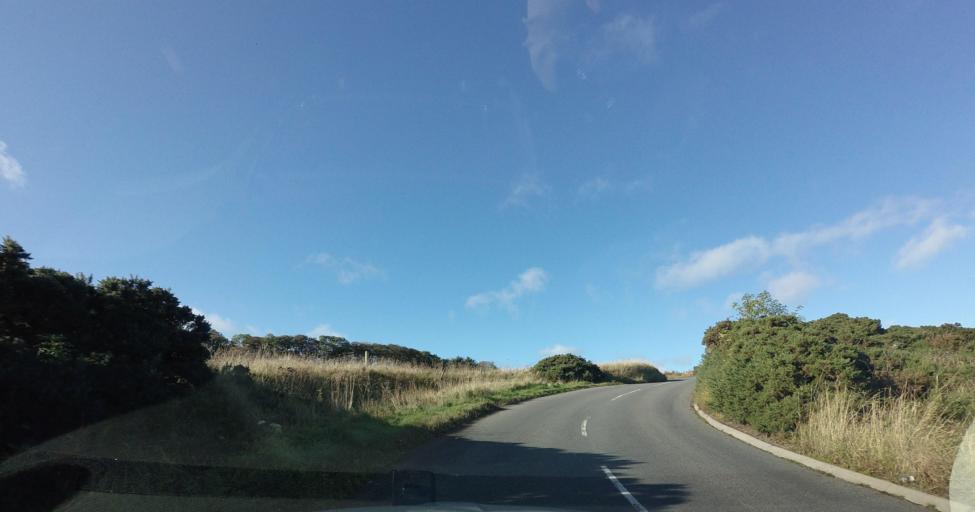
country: GB
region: Scotland
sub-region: Aberdeenshire
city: Macduff
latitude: 57.6607
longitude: -2.3581
